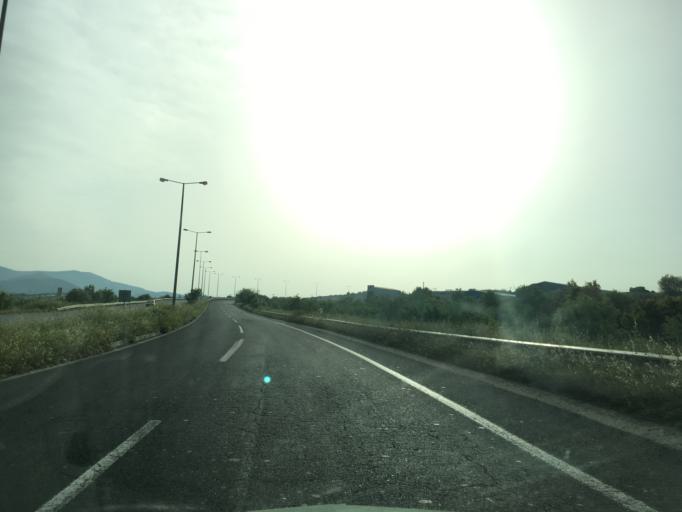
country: GR
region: Thessaly
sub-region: Nomos Magnisias
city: Nea Ionia
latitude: 39.3826
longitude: 22.8597
